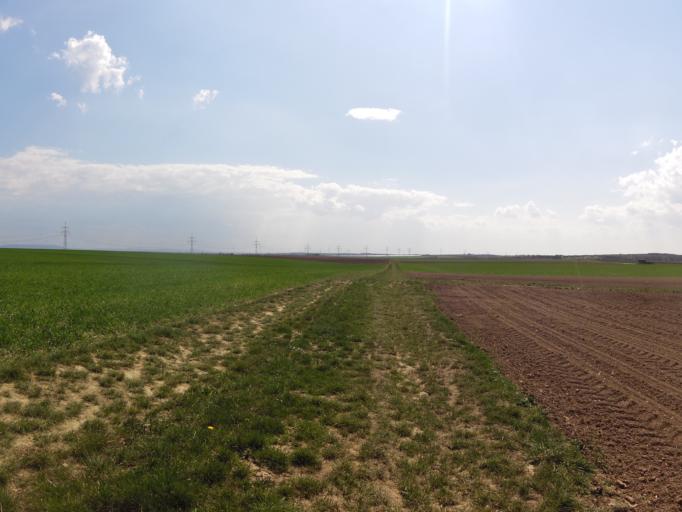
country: DE
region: Bavaria
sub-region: Regierungsbezirk Unterfranken
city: Oberpleichfeld
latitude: 49.8505
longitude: 10.0824
